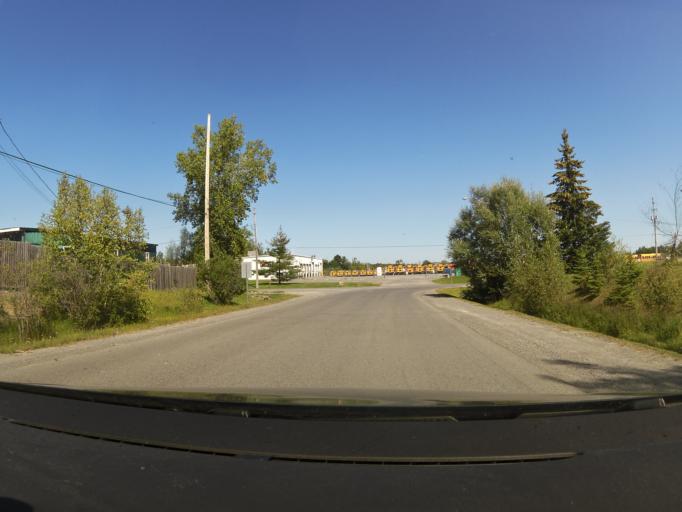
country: CA
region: Ontario
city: Bells Corners
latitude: 45.2917
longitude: -75.9779
